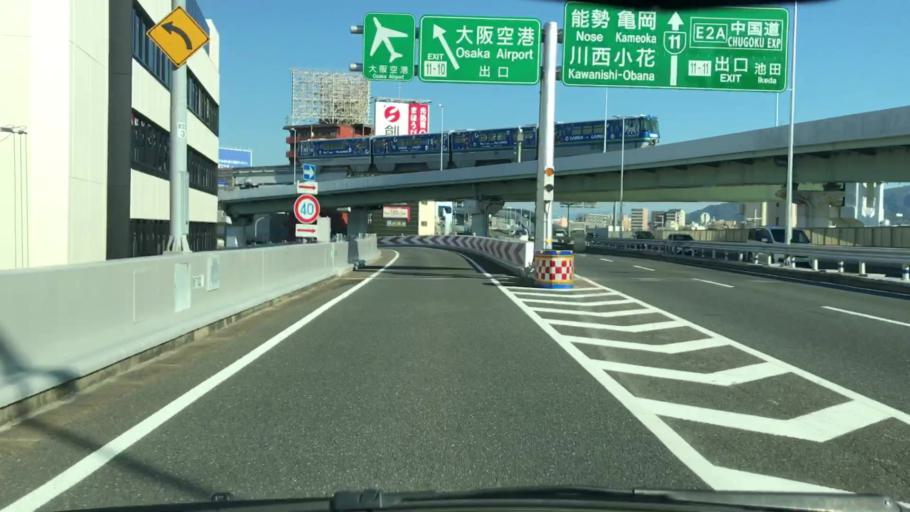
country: JP
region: Osaka
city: Toyonaka
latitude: 34.7886
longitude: 135.4480
